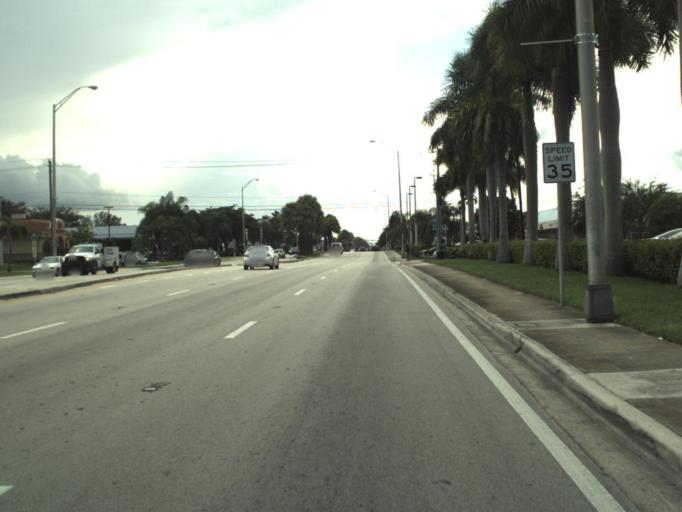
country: US
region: Florida
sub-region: Miami-Dade County
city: North Miami Beach
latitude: 25.9260
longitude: -80.1651
